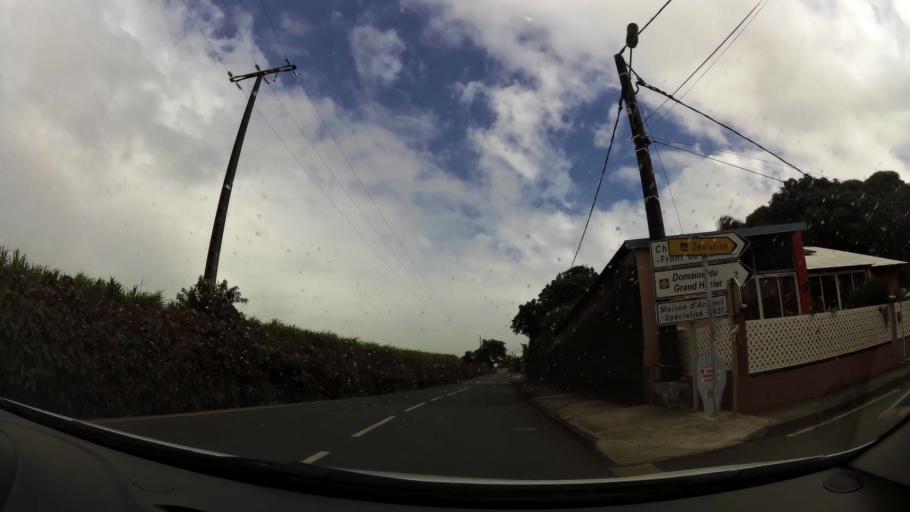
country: RE
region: Reunion
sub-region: Reunion
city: Sainte-Suzanne
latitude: -20.9078
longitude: 55.5985
